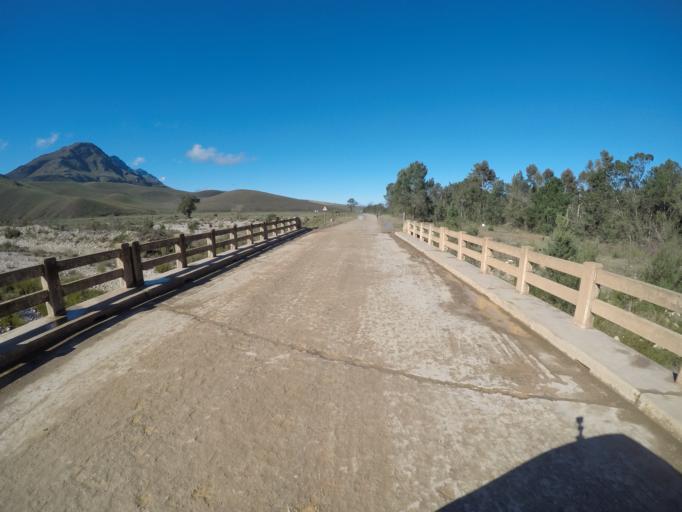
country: ZA
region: Western Cape
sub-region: Overberg District Municipality
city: Caledon
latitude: -34.0532
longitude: 19.6140
